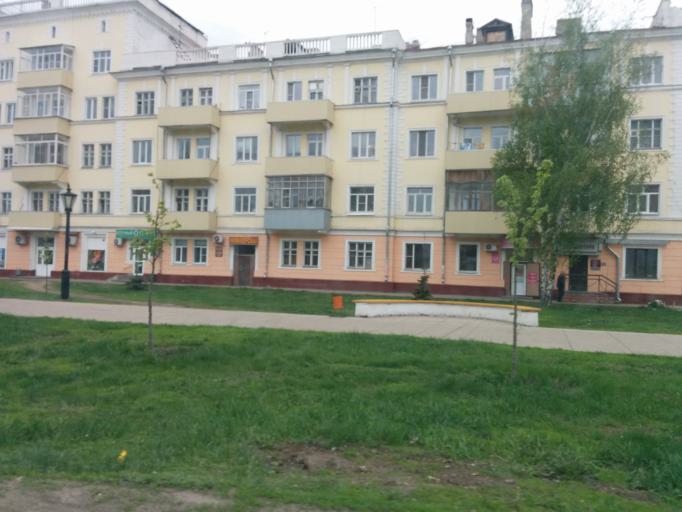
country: RU
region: Tambov
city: Tambov
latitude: 52.7205
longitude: 41.4376
